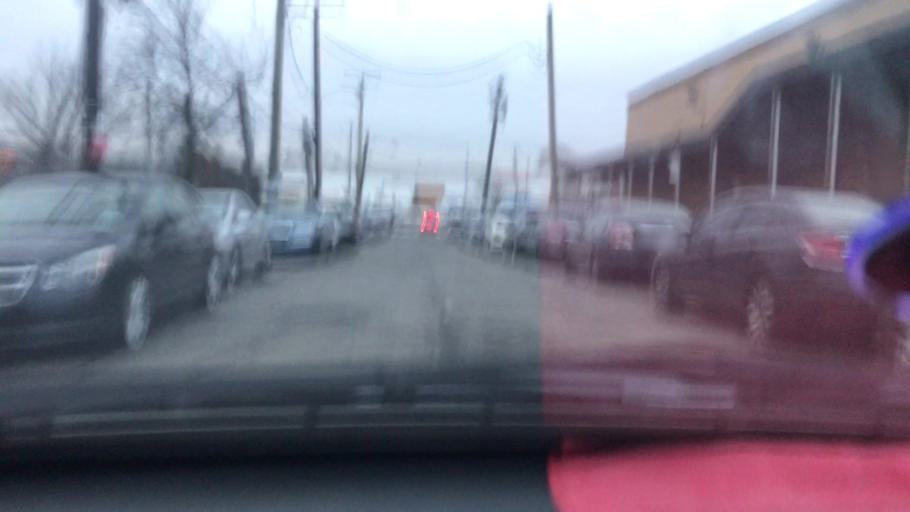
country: US
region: Maryland
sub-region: Prince George's County
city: Mount Rainier
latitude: 38.9203
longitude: -76.9715
